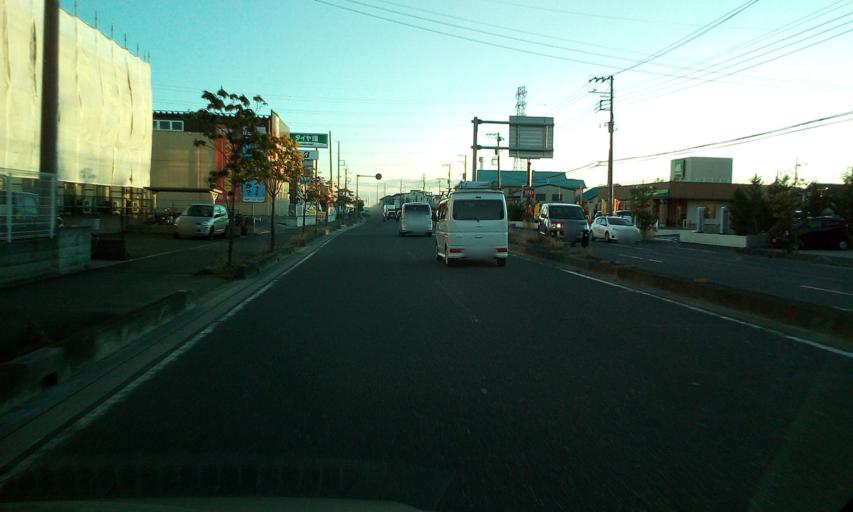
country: JP
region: Saitama
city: Yoshikawa
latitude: 35.8645
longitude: 139.8484
